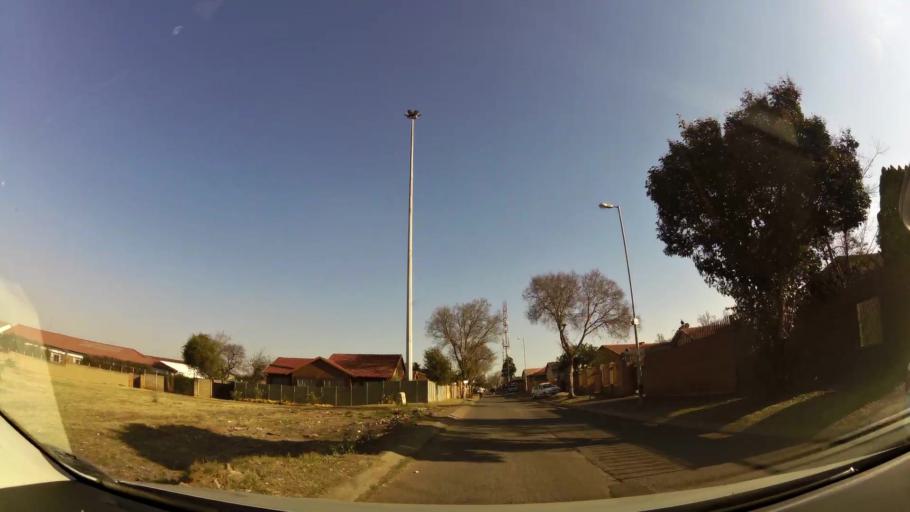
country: ZA
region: Gauteng
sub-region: City of Johannesburg Metropolitan Municipality
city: Soweto
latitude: -26.2683
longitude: 27.8771
